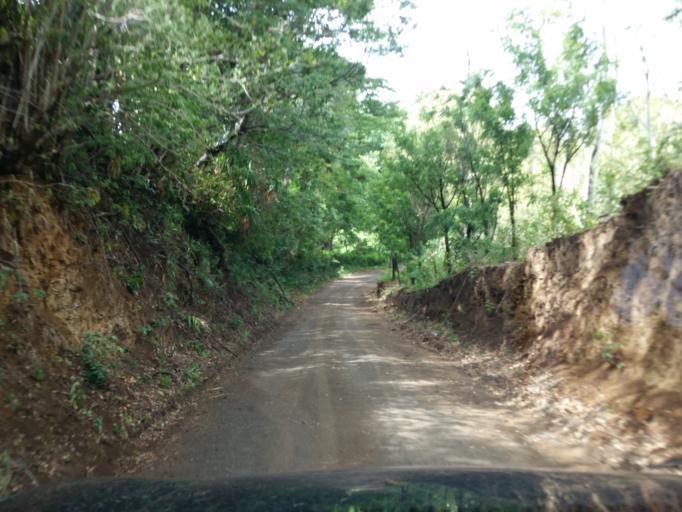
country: NI
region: Managua
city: El Crucero
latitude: 12.0056
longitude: -86.3509
